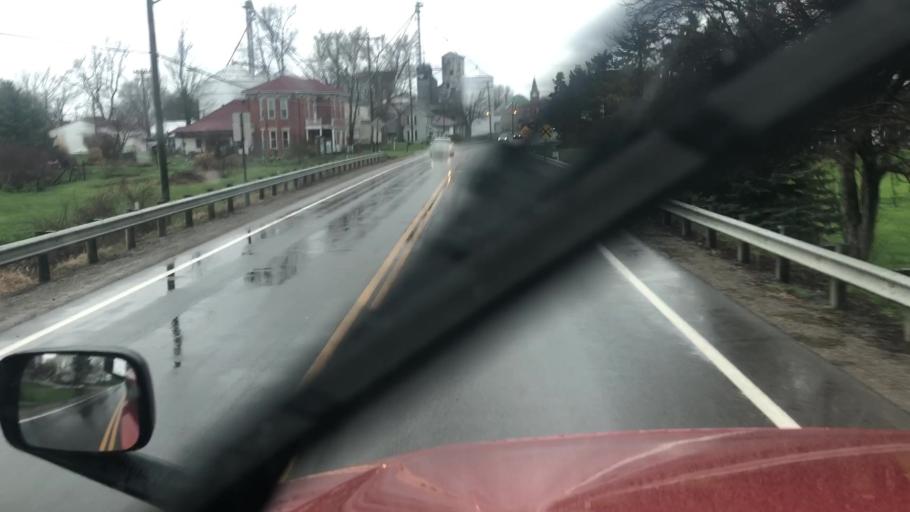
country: US
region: Ohio
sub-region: Hardin County
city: Kenton
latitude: 40.5315
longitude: -83.5192
